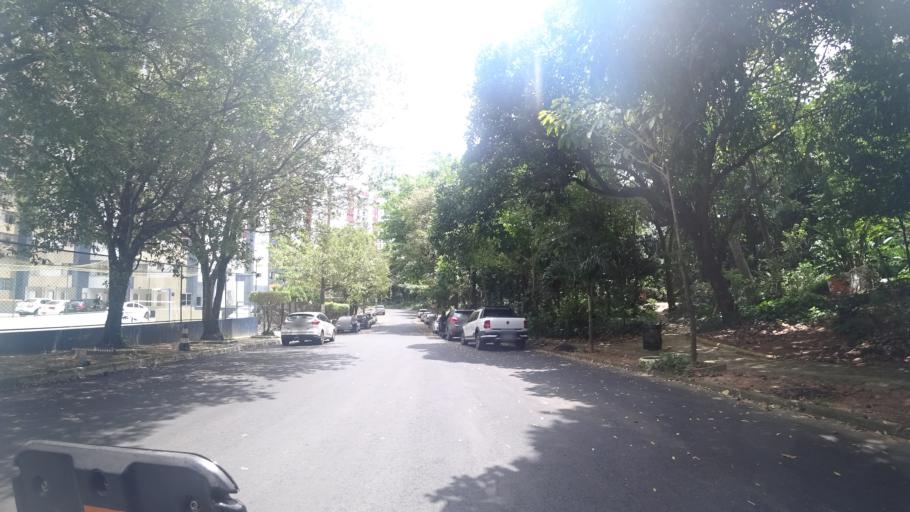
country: BR
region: Bahia
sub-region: Salvador
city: Salvador
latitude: -12.9932
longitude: -38.4713
